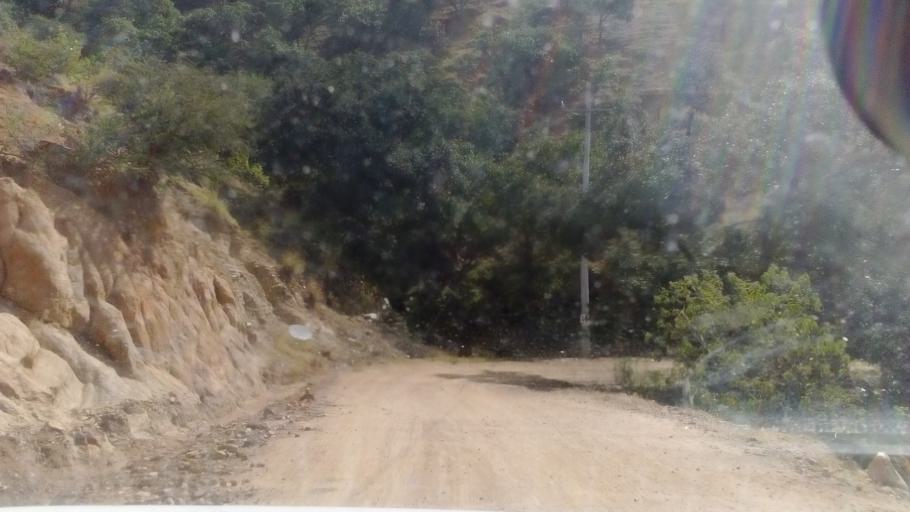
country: MX
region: Guanajuato
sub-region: Silao de la Victoria
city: San Francisco (Banos de Agua Caliente)
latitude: 21.1647
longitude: -101.4611
